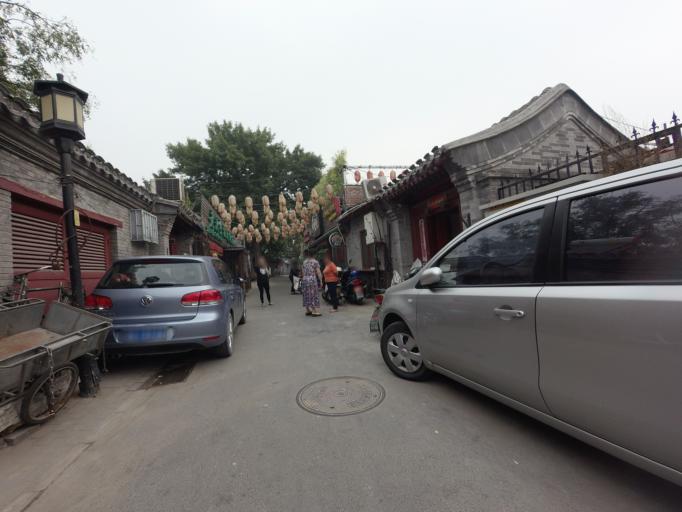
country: CN
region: Beijing
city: Jingshan
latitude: 39.9386
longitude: 116.3881
